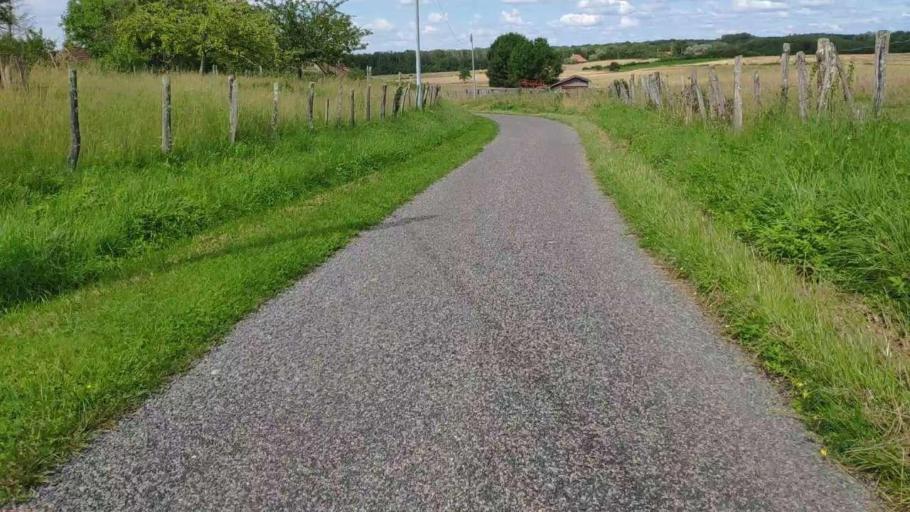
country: FR
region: Franche-Comte
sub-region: Departement du Jura
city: Bletterans
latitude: 46.8233
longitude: 5.4516
